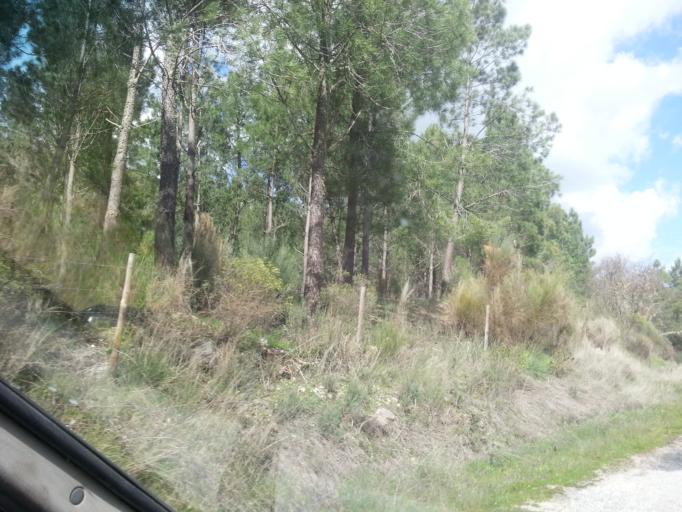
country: PT
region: Guarda
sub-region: Fornos de Algodres
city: Fornos de Algodres
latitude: 40.6509
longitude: -7.5015
